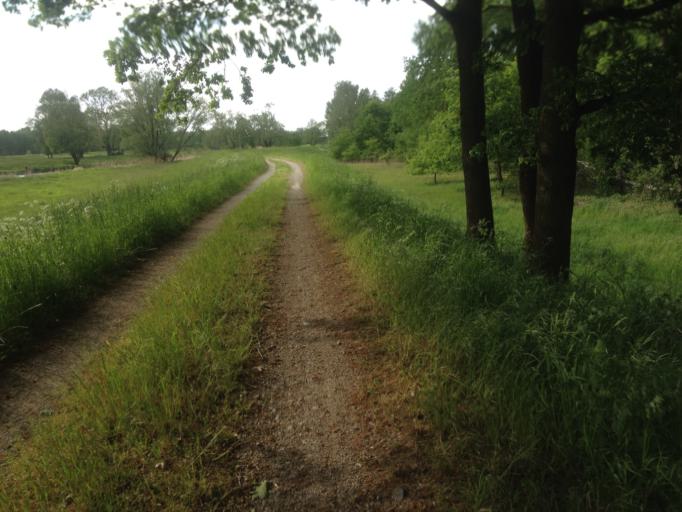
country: DE
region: Brandenburg
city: Drehnow
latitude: 51.8380
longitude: 14.3439
